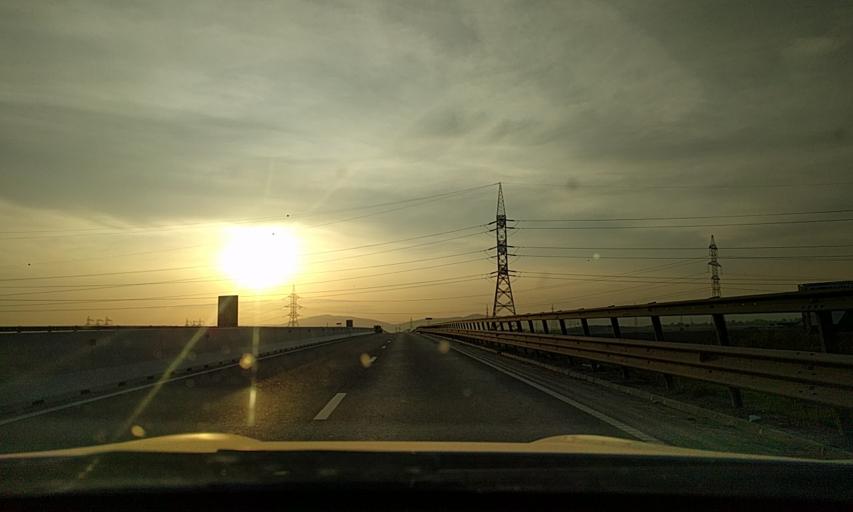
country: RO
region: Brasov
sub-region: Comuna Sanpetru
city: Sanpetru
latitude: 45.6885
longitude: 25.6459
